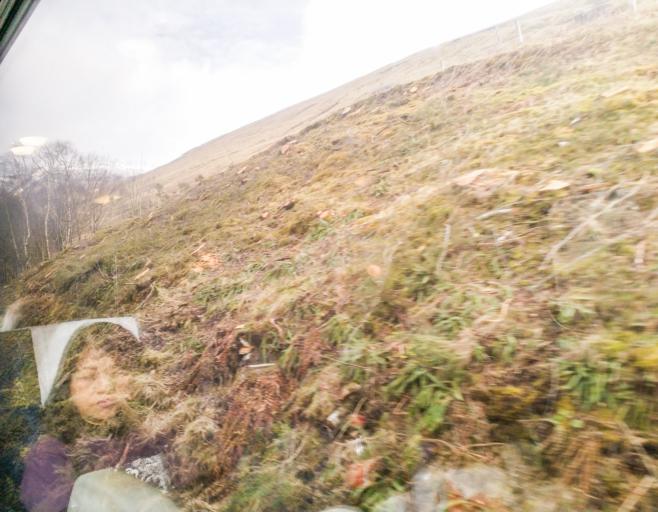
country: GB
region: Scotland
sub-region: Highland
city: Spean Bridge
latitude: 56.8045
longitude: -4.7192
